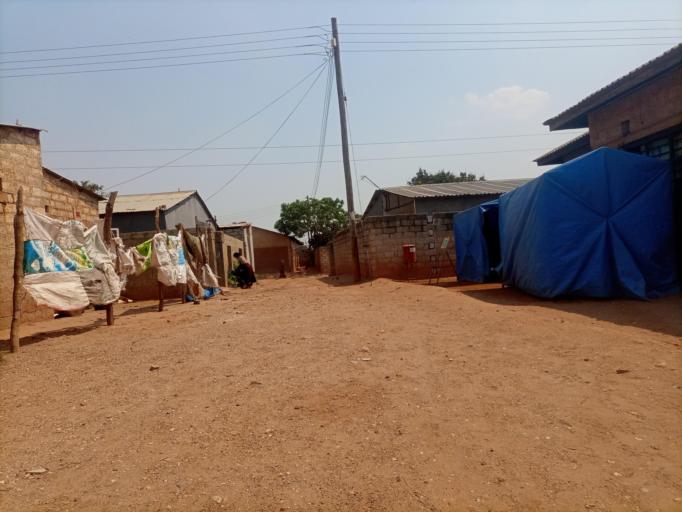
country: ZM
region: Lusaka
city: Lusaka
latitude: -15.4033
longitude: 28.3782
